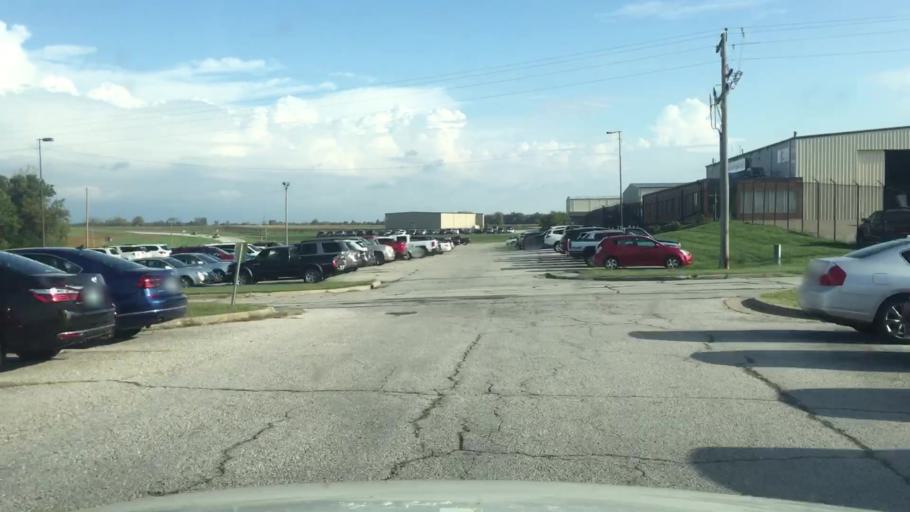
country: US
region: Missouri
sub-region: Boone County
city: Ashland
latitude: 38.8183
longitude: -92.2219
